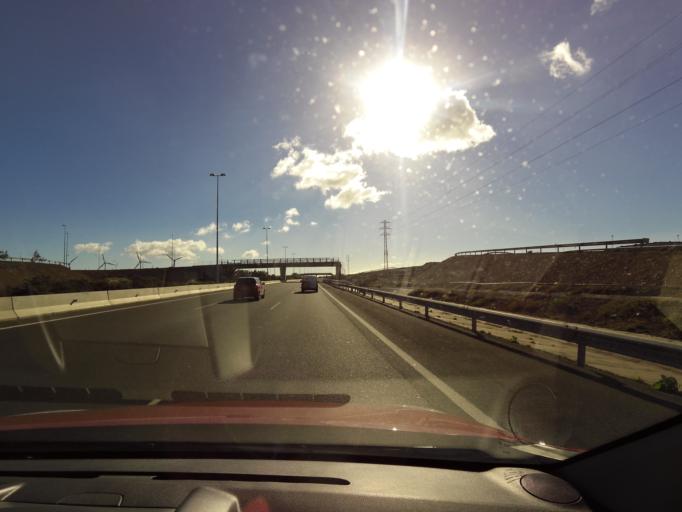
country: ES
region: Canary Islands
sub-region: Provincia de Las Palmas
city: Cruce de Arinaga
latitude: 27.8544
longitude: -15.4299
